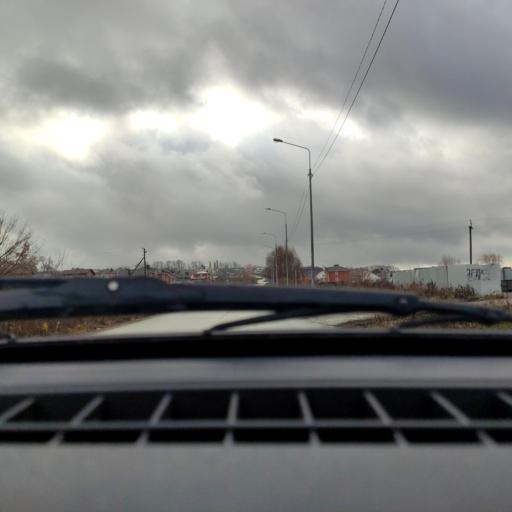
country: RU
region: Bashkortostan
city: Kabakovo
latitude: 54.6386
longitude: 56.0766
